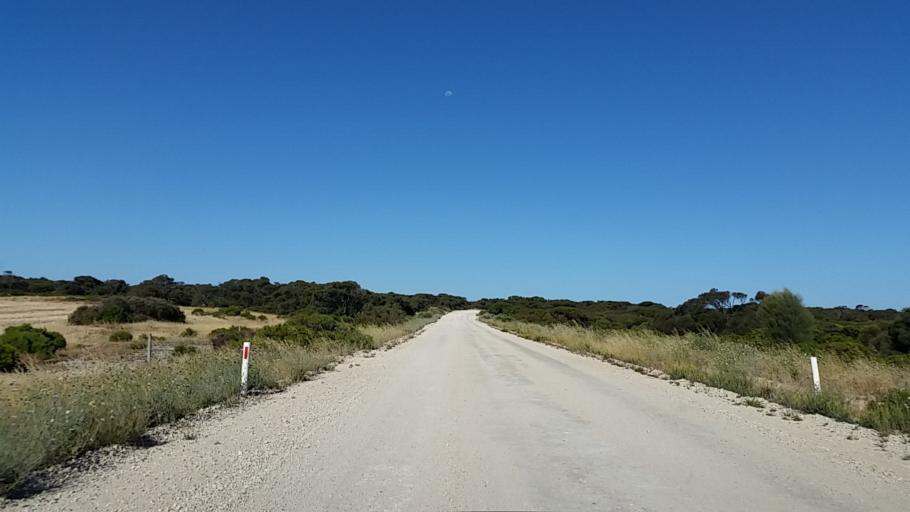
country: AU
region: South Australia
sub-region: Yorke Peninsula
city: Honiton
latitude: -35.2198
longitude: 137.0806
